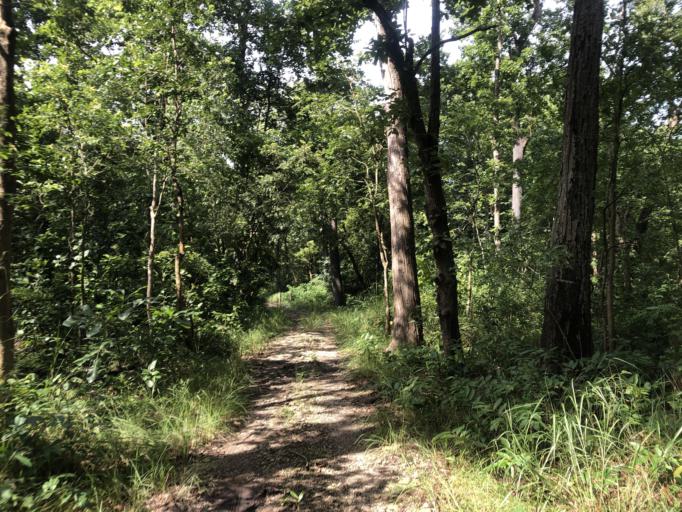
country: NP
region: Far Western
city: Tikapur
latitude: 28.5418
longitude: 81.2867
